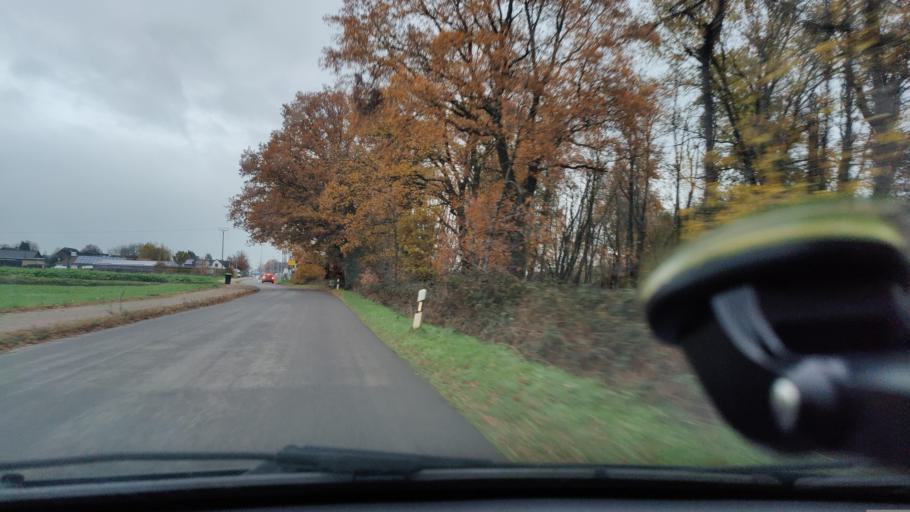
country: DE
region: North Rhine-Westphalia
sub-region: Regierungsbezirk Dusseldorf
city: Kamp-Lintfort
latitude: 51.5315
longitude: 6.5488
